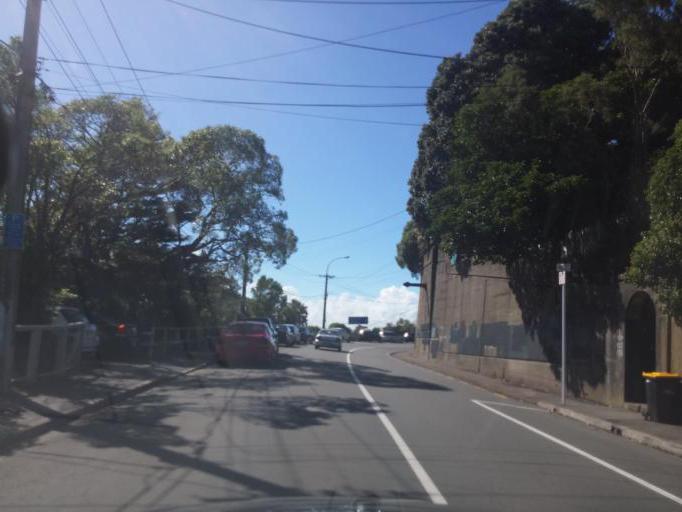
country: NZ
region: Wellington
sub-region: Wellington City
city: Kelburn
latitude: -41.2868
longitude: 174.7589
